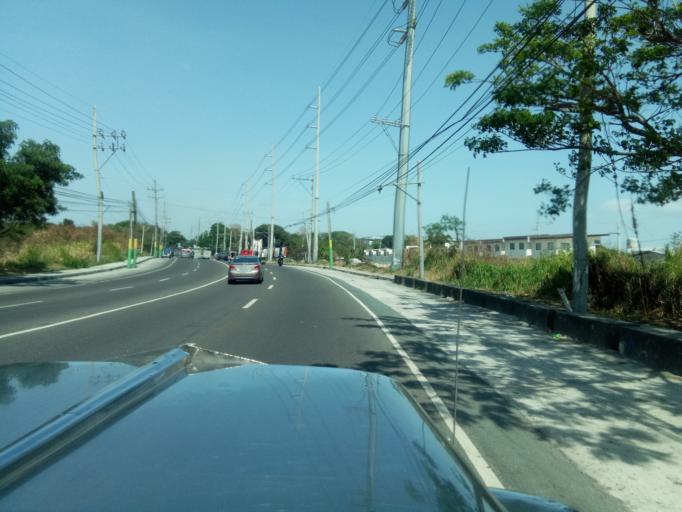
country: PH
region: Calabarzon
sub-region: Province of Cavite
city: Dasmarinas
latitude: 14.2942
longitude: 120.9411
